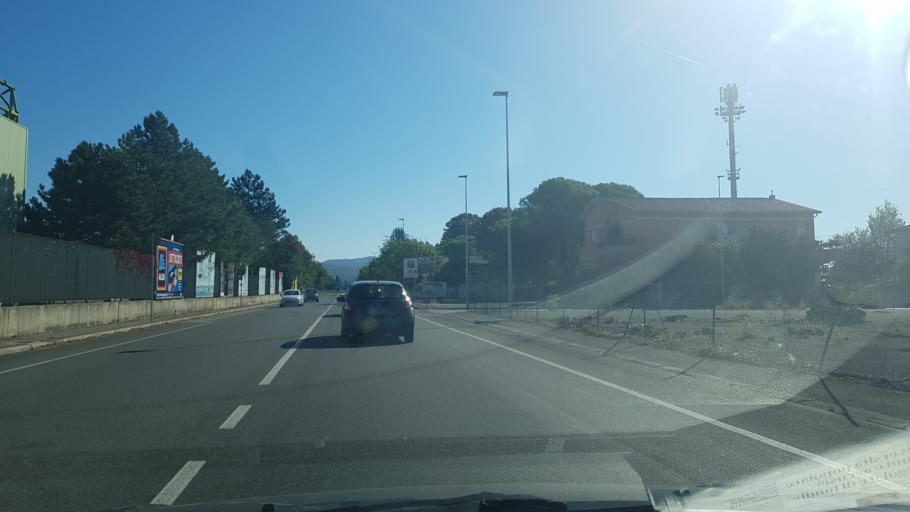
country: IT
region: Friuli Venezia Giulia
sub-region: Provincia di Gorizia
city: Monfalcone
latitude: 45.8024
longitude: 13.5419
